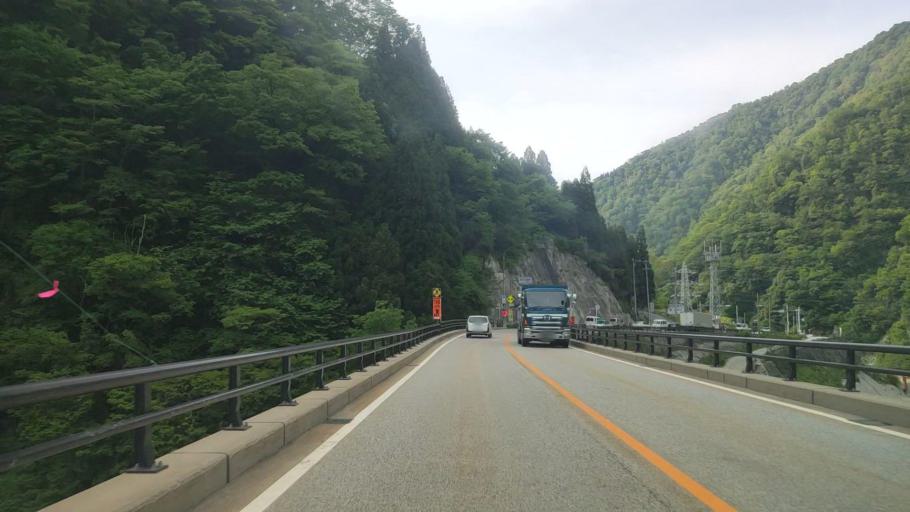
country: JP
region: Gifu
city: Takayama
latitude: 36.3645
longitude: 137.2846
